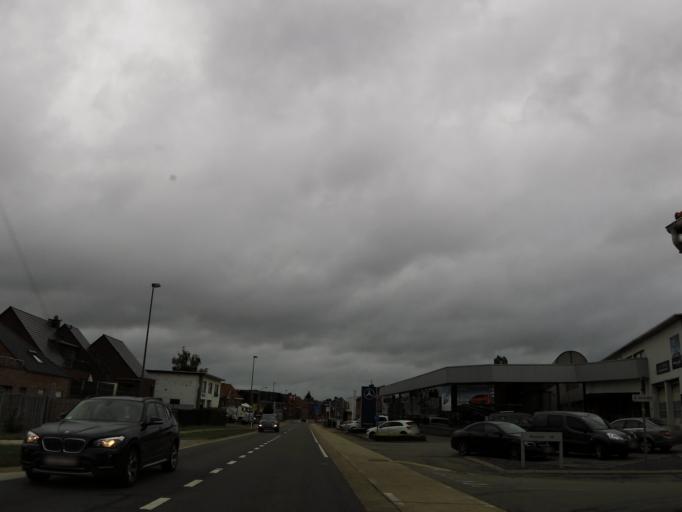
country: BE
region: Flanders
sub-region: Provincie Limburg
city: Bree
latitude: 51.1349
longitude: 5.5932
